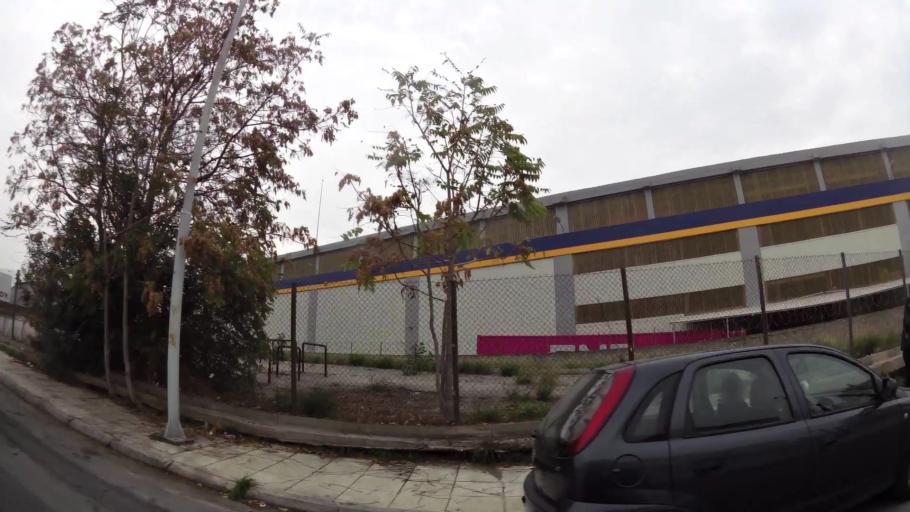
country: GR
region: Attica
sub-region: Nomarchia Athinas
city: Aigaleo
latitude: 37.9753
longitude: 23.6794
